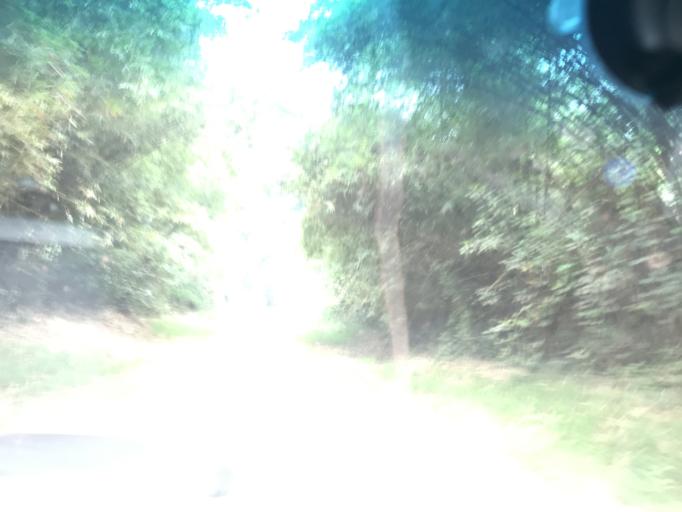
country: CD
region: Eastern Province
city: Buta
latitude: 2.8775
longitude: 24.4771
